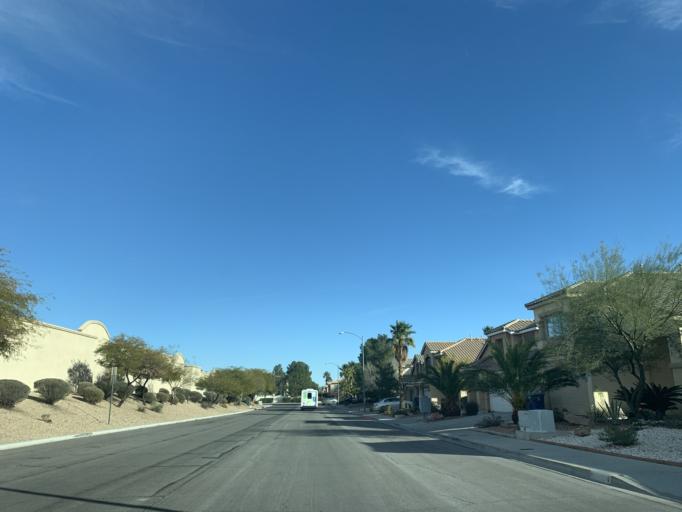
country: US
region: Nevada
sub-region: Clark County
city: Summerlin South
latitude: 36.1280
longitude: -115.2988
